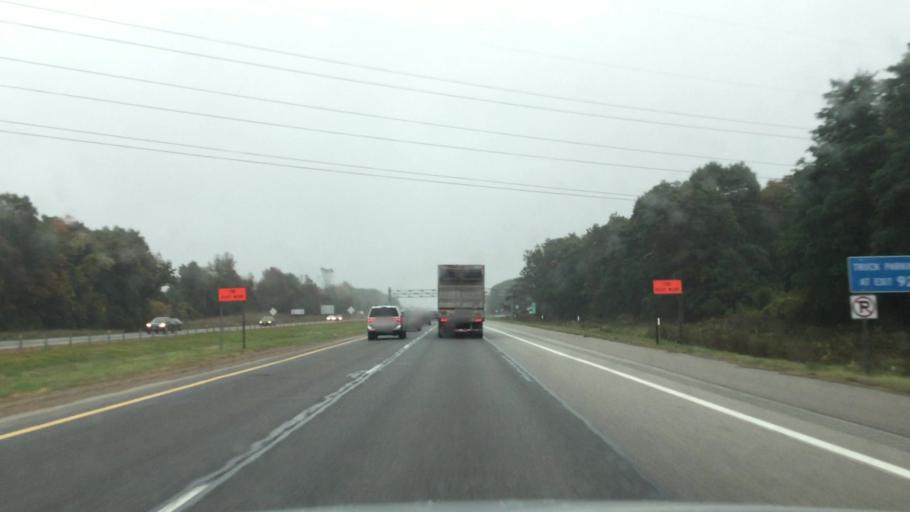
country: US
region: Michigan
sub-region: Kalamazoo County
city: Westwood
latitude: 42.2375
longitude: -85.6676
